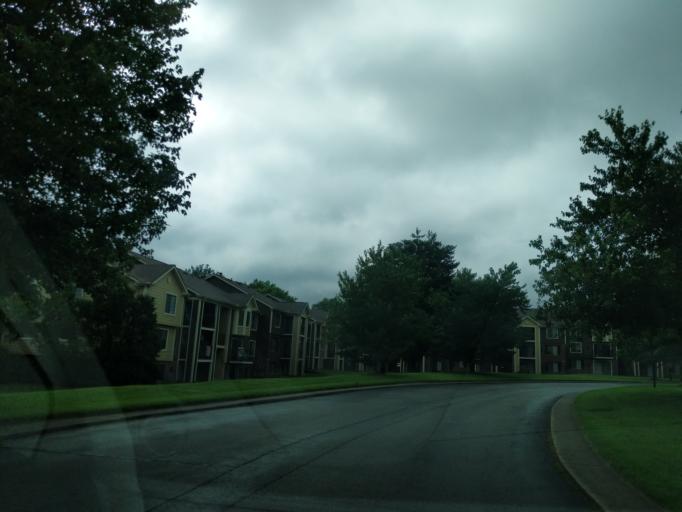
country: US
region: Tennessee
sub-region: Davidson County
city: Lakewood
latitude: 36.1734
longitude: -86.6106
